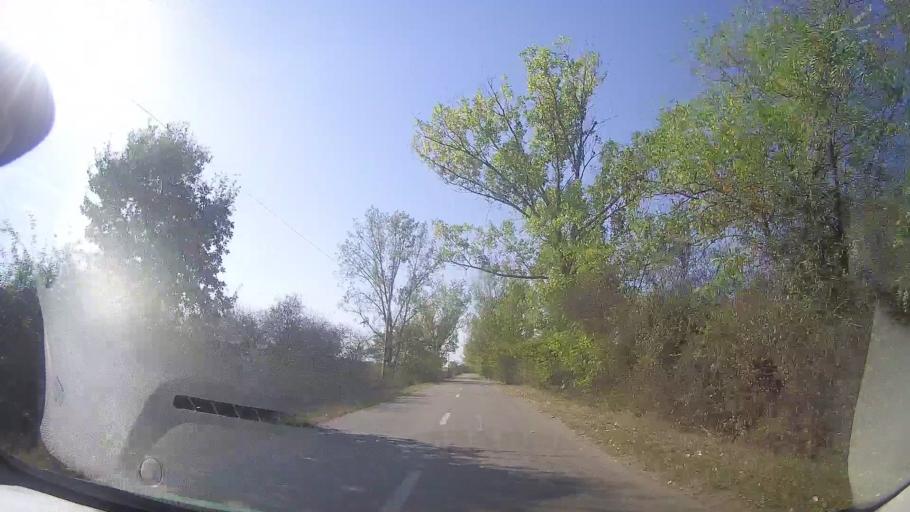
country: RO
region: Timis
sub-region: Comuna Secas
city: Secas
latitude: 45.8601
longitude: 21.8042
